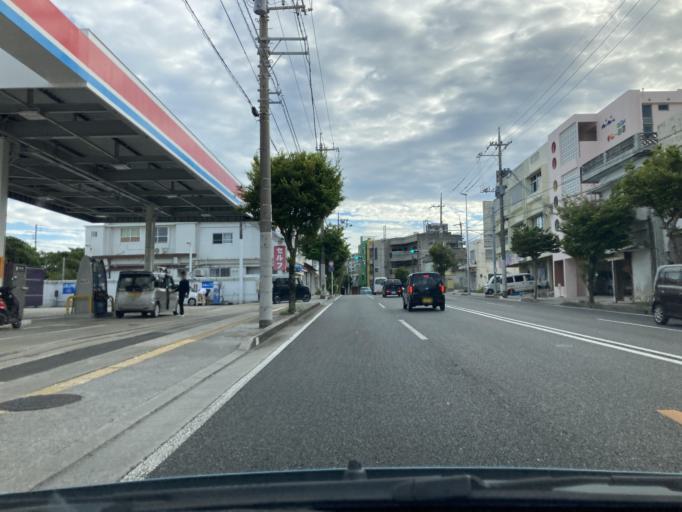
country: JP
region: Okinawa
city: Okinawa
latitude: 26.3435
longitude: 127.8137
